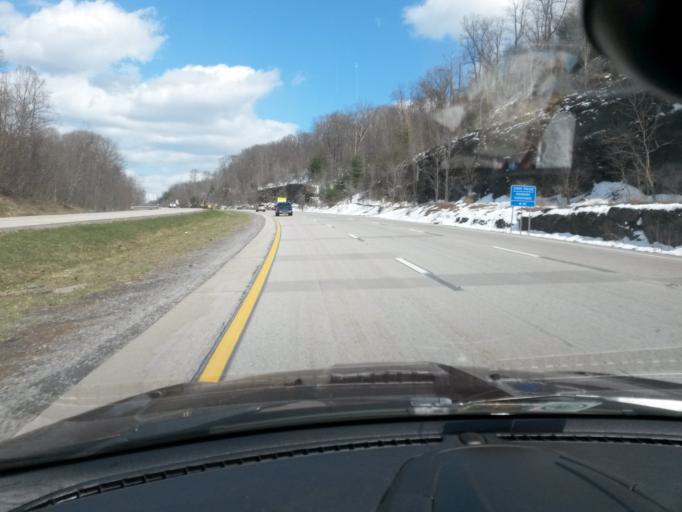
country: US
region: West Virginia
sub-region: Raleigh County
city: Beaver
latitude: 37.7378
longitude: -81.1762
